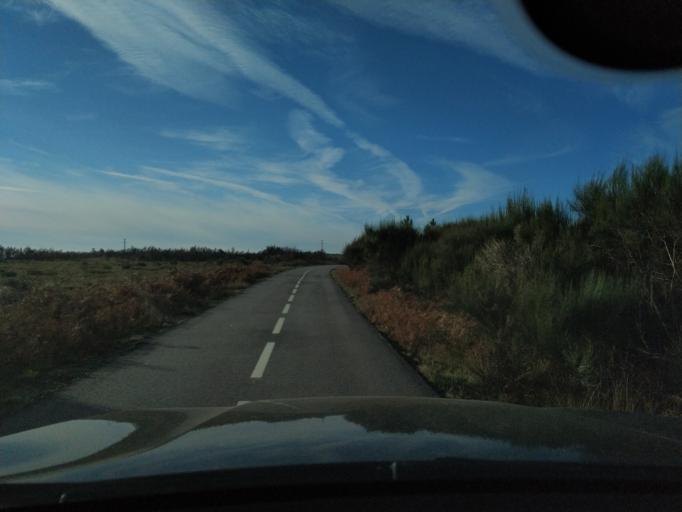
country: PT
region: Vila Real
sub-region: Sabrosa
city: Sabrosa
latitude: 41.3003
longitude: -7.6097
